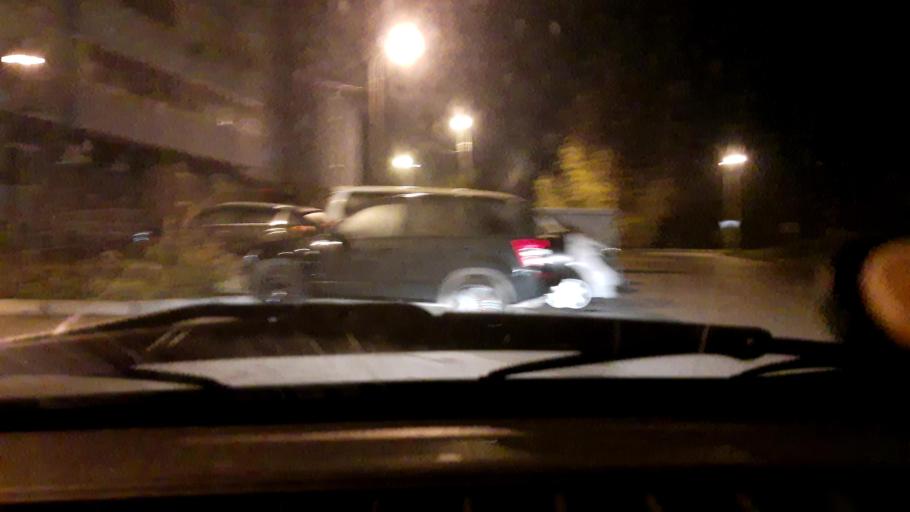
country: RU
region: Bashkortostan
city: Ufa
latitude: 54.7608
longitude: 56.0486
